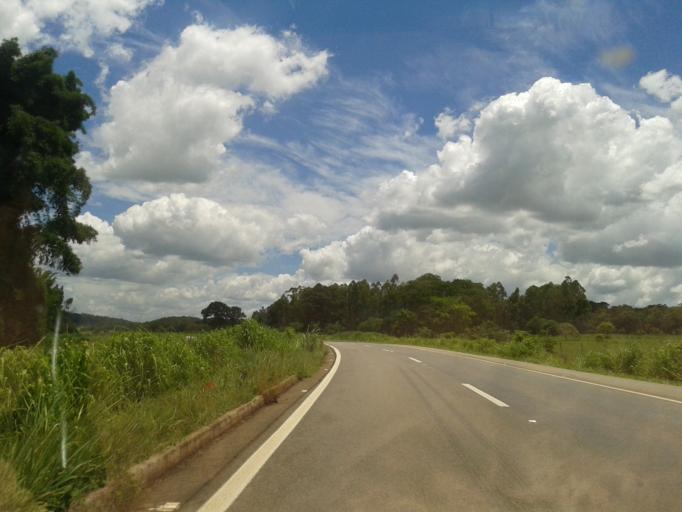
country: BR
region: Goias
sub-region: Neropolis
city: Neropolis
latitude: -16.2783
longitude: -49.2954
